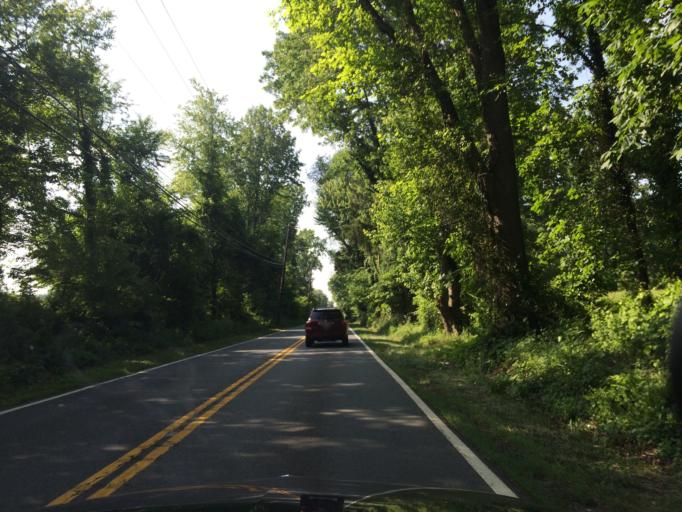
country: US
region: Maryland
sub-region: Montgomery County
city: Olney
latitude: 39.1843
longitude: -77.0631
